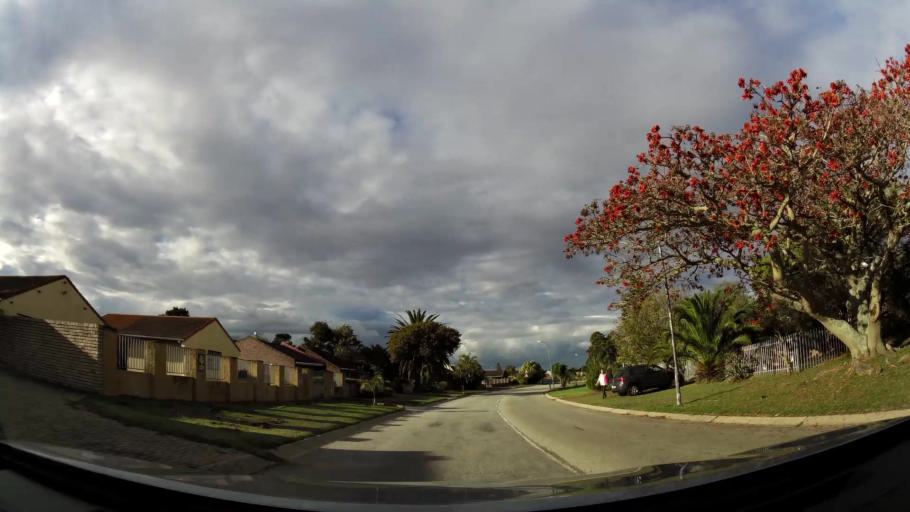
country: ZA
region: Eastern Cape
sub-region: Nelson Mandela Bay Metropolitan Municipality
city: Port Elizabeth
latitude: -33.9541
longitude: 25.4816
